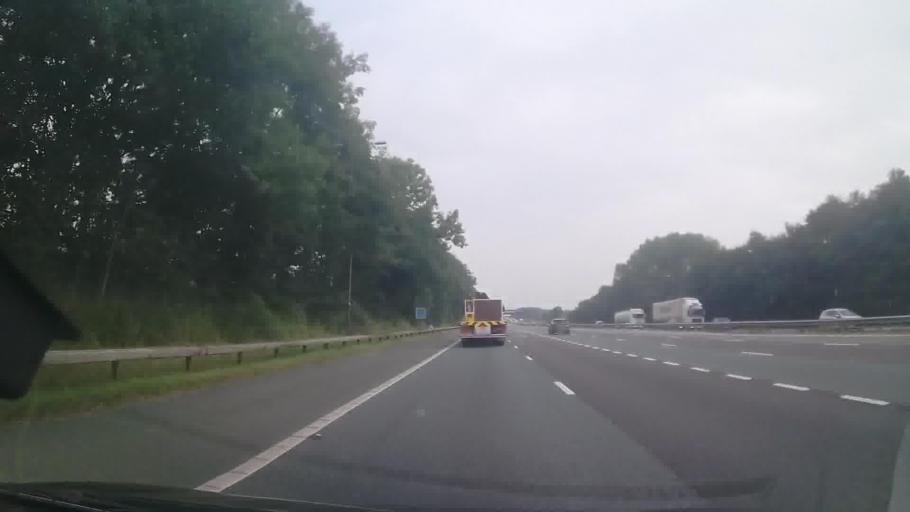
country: GB
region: England
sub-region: Warrington
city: Appleton Thorn
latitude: 53.3487
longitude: -2.5189
